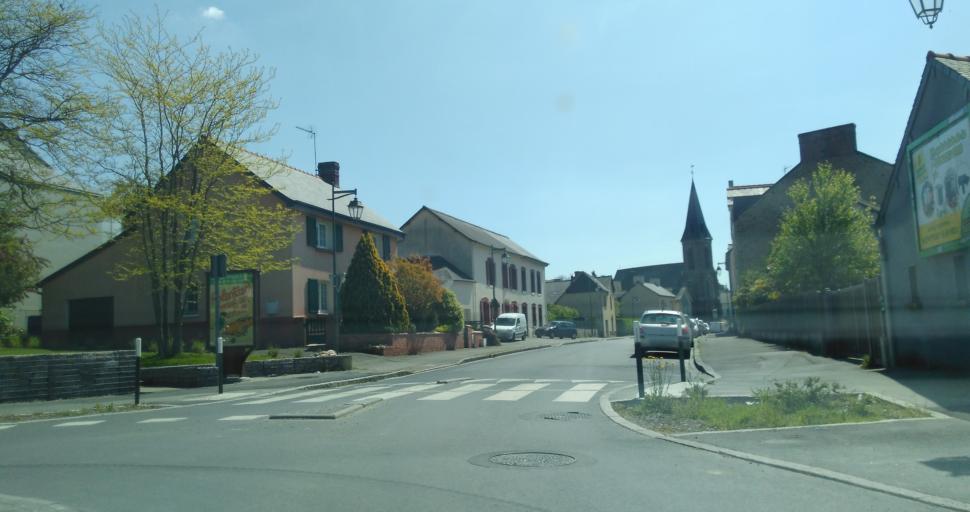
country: FR
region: Brittany
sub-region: Departement d'Ille-et-Vilaine
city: Saint-Gilles
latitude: 48.1272
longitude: -1.8191
